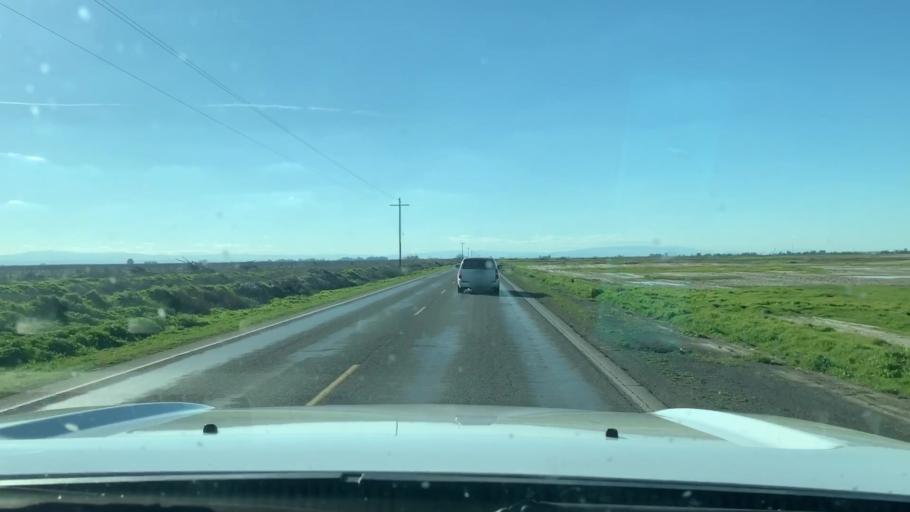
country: US
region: California
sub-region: Kings County
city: Armona
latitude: 36.2111
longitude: -119.7184
